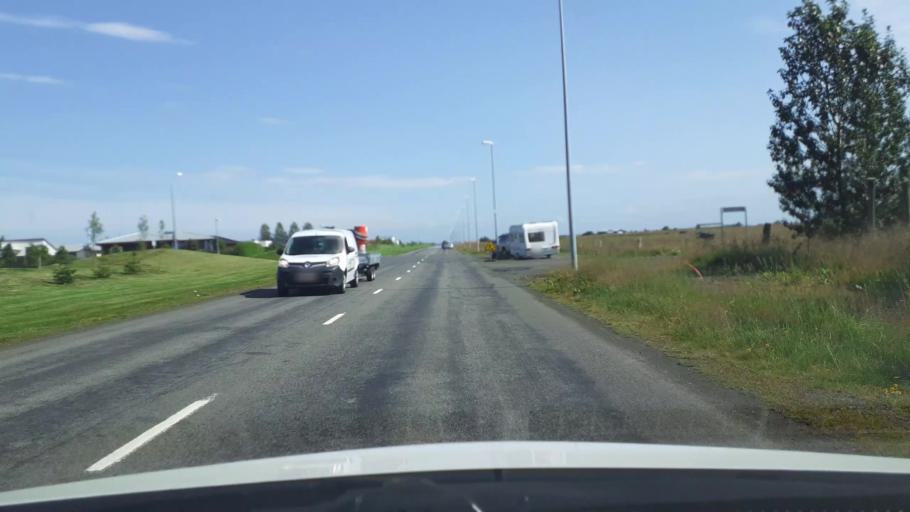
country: IS
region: South
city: Selfoss
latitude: 63.9225
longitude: -21.0011
